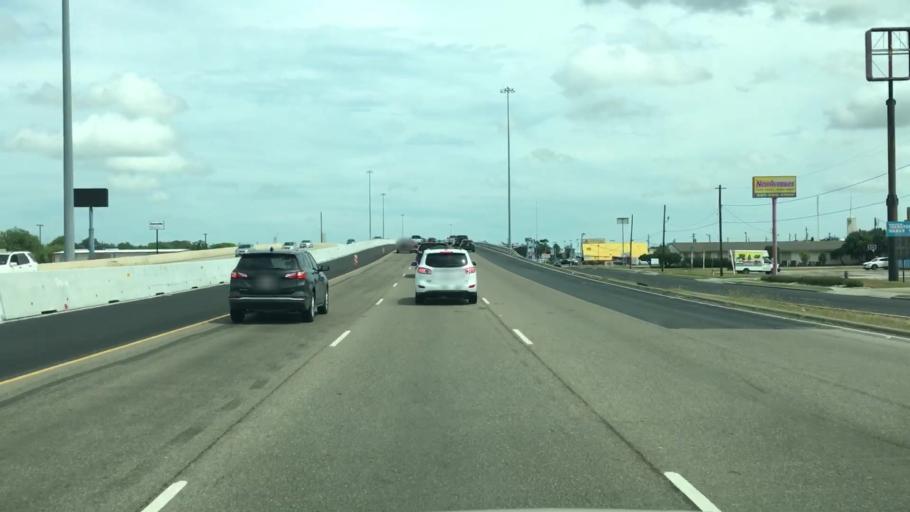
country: US
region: Texas
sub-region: Nueces County
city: Corpus Christi
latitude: 27.7263
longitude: -97.4084
